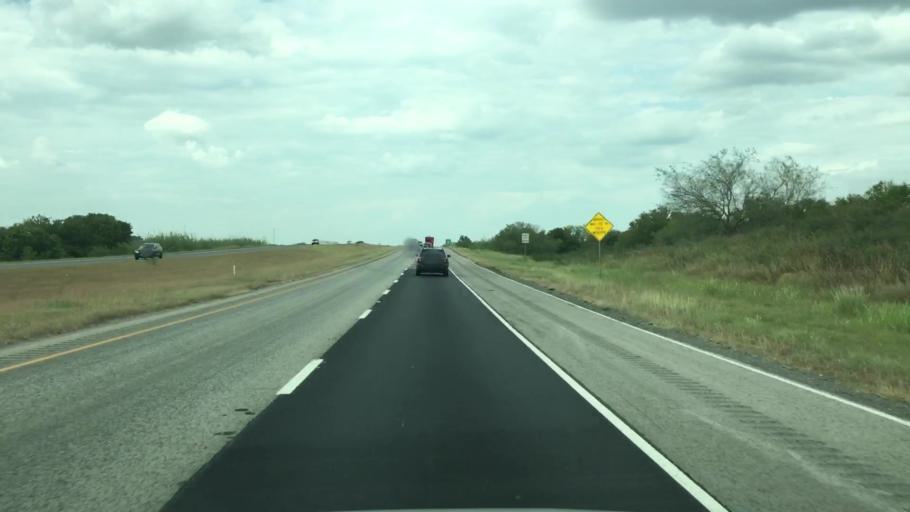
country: US
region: Texas
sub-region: Atascosa County
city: Pleasanton
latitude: 29.0834
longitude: -98.4328
